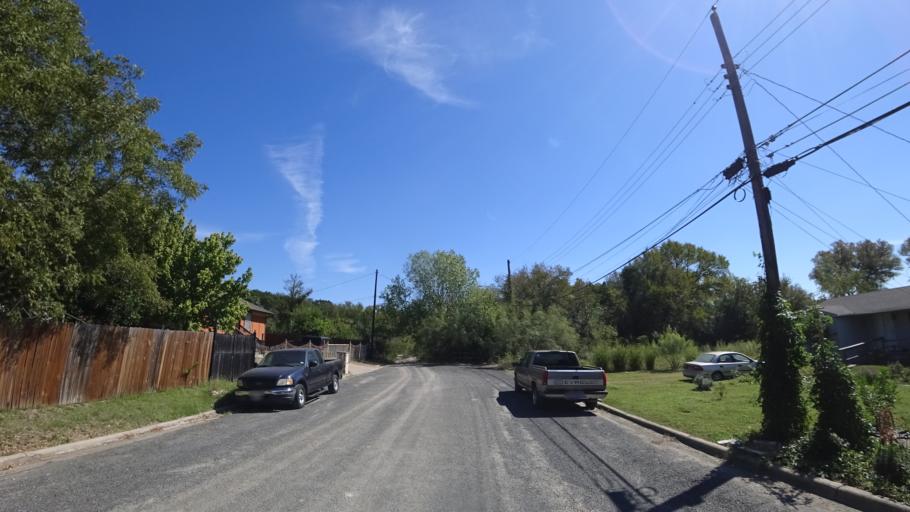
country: US
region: Texas
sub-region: Travis County
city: Austin
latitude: 30.2711
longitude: -97.6791
